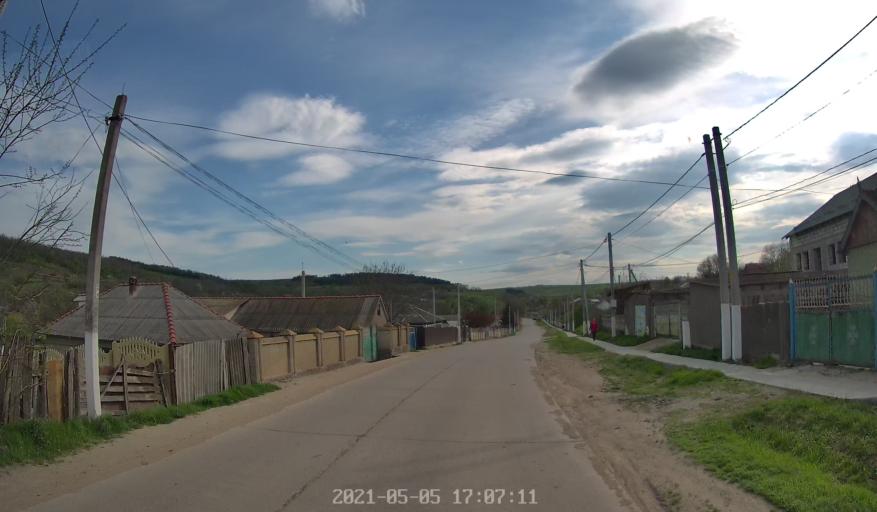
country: MD
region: Chisinau
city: Vadul lui Voda
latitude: 47.0147
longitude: 29.1365
